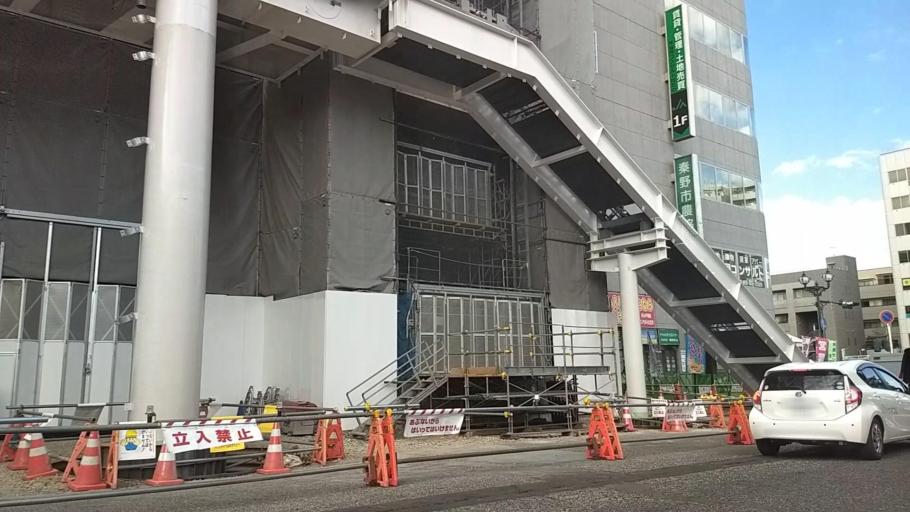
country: JP
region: Kanagawa
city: Hadano
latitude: 35.3708
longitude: 139.2265
